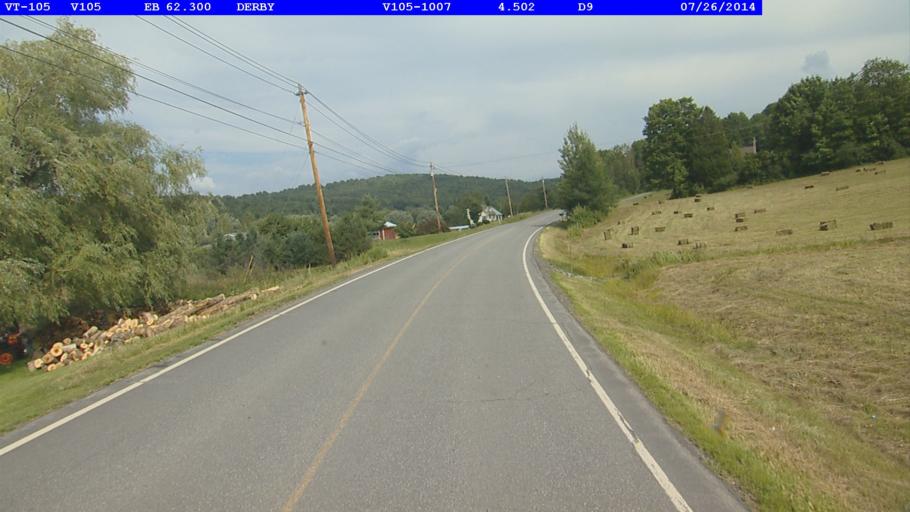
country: US
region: Vermont
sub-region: Orleans County
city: Newport
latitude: 44.9065
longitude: -72.0834
